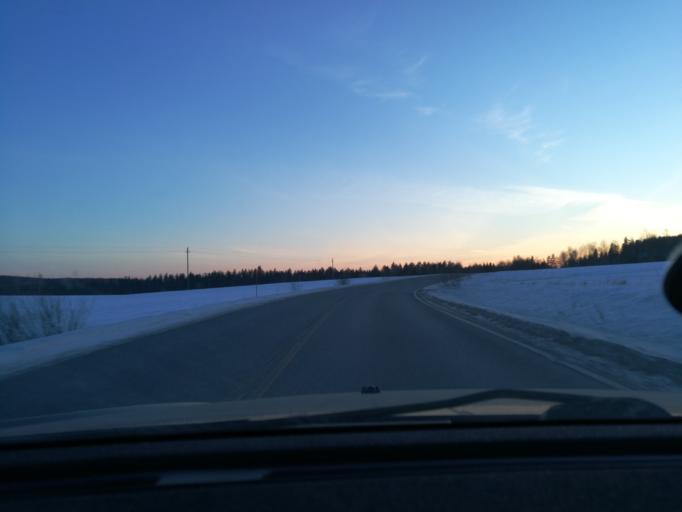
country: FI
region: Uusimaa
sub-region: Helsinki
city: Vihti
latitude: 60.4250
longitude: 24.3689
